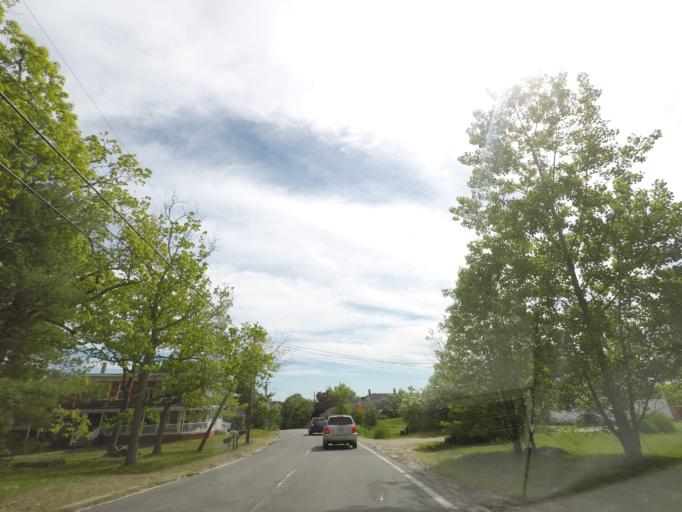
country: US
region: Maine
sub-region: Sagadahoc County
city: Richmond
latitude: 44.0947
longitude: -69.7897
